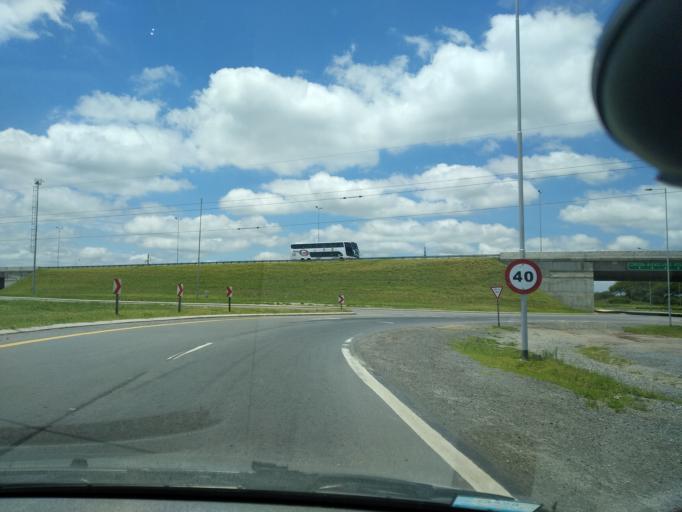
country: AR
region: Cordoba
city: Alta Gracia
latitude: -31.6522
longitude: -64.3166
